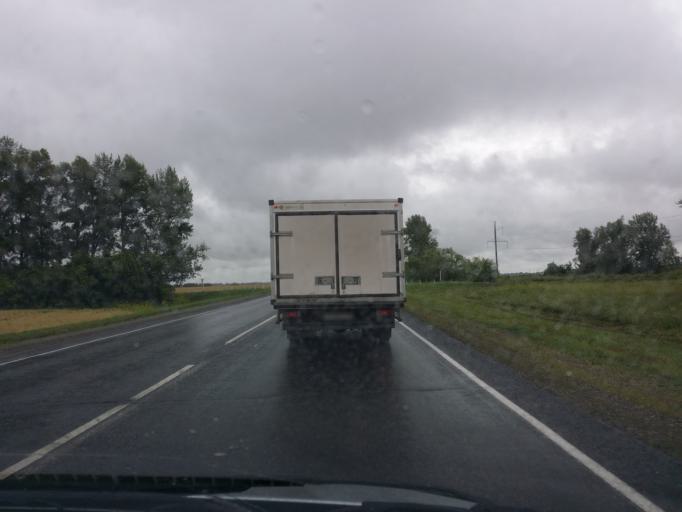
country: RU
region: Altai Krai
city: Zonal'noye
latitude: 52.7328
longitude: 84.9602
